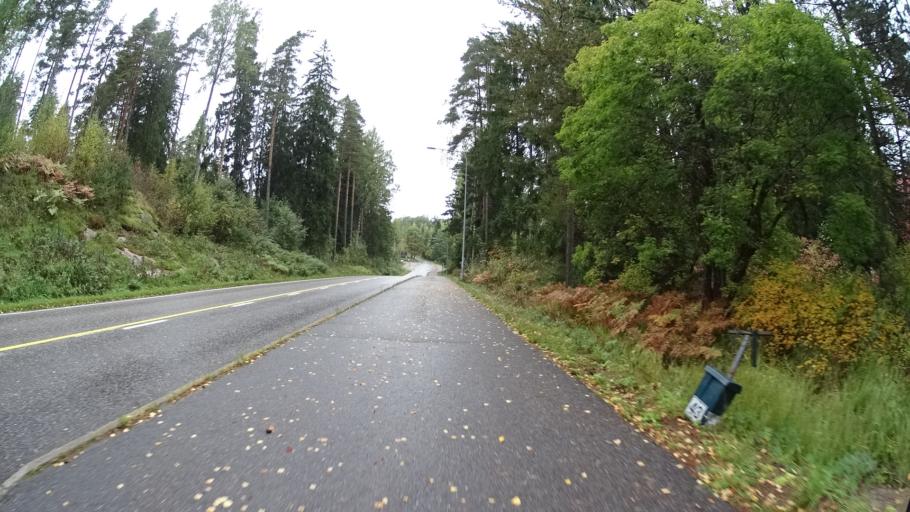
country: FI
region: Uusimaa
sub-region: Helsinki
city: Espoo
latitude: 60.2486
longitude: 24.6557
